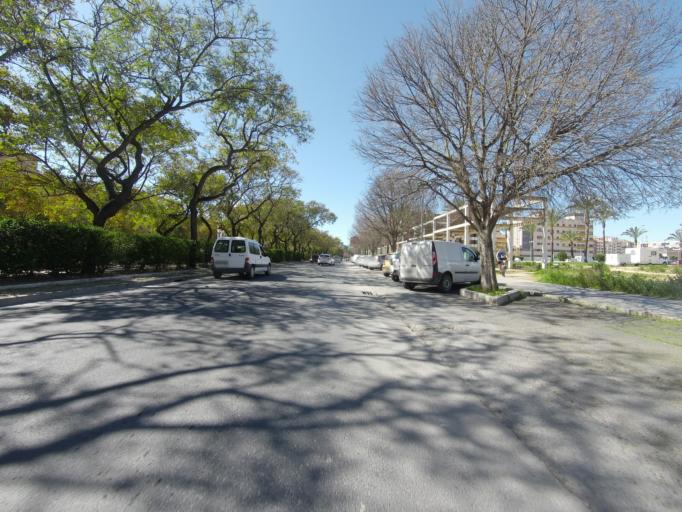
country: ES
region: Andalusia
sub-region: Provincia de Huelva
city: Huelva
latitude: 37.2661
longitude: -6.9381
